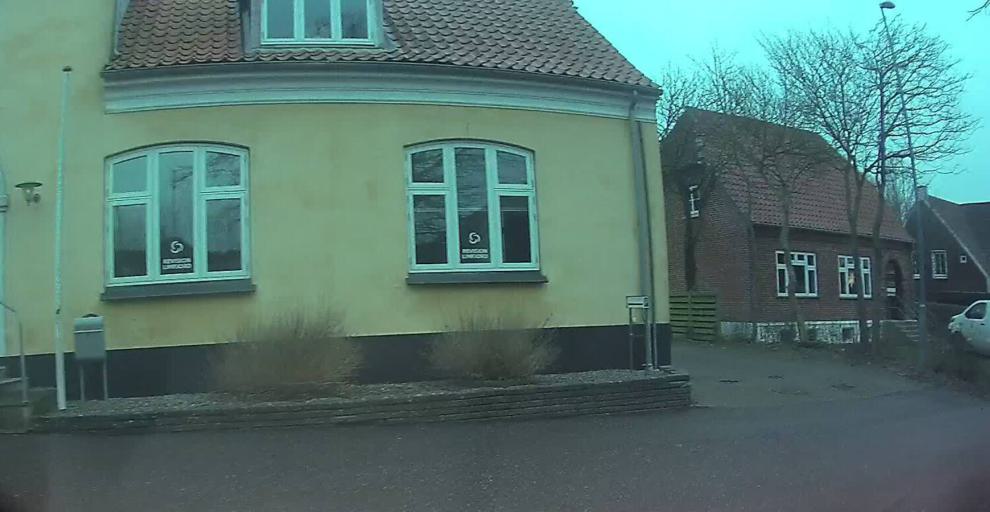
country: DK
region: North Denmark
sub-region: Thisted Kommune
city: Hurup
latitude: 56.7509
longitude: 8.4222
